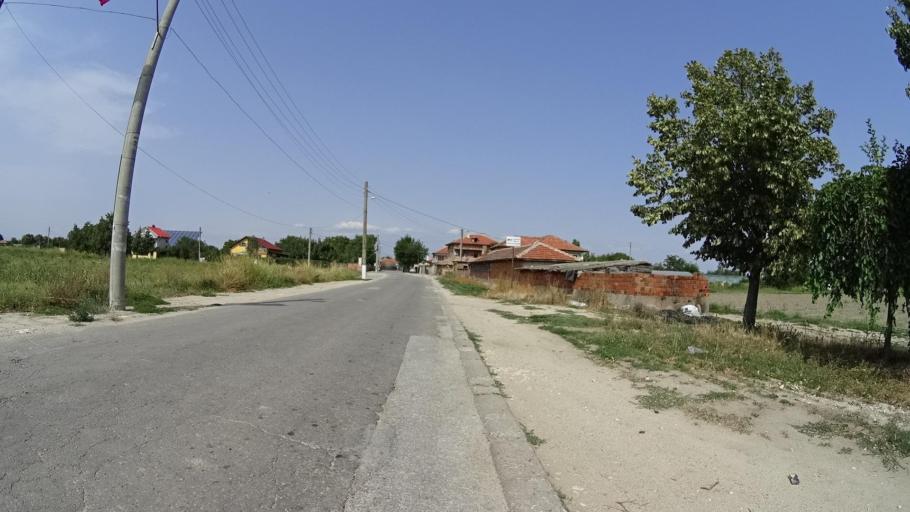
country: BG
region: Plovdiv
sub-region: Obshtina Plovdiv
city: Plovdiv
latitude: 42.2370
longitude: 24.7890
